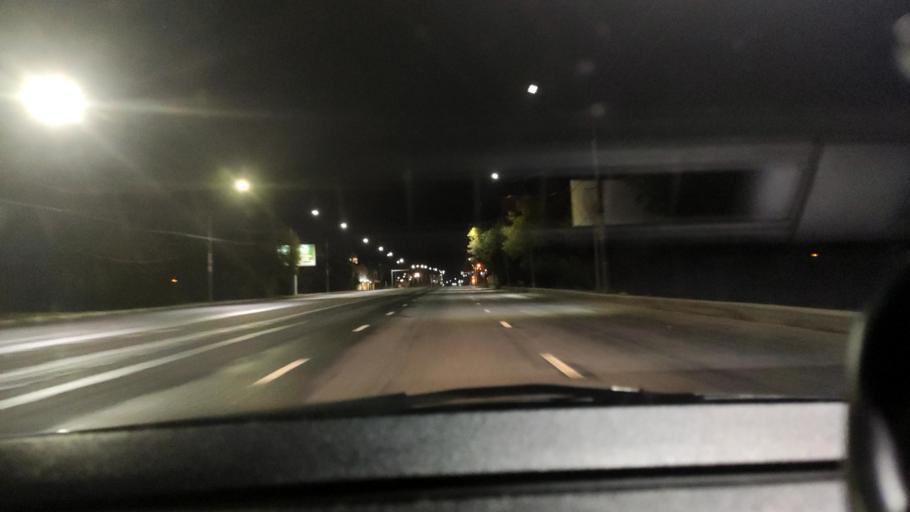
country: RU
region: Voronezj
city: Voronezh
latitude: 51.6384
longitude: 39.2069
